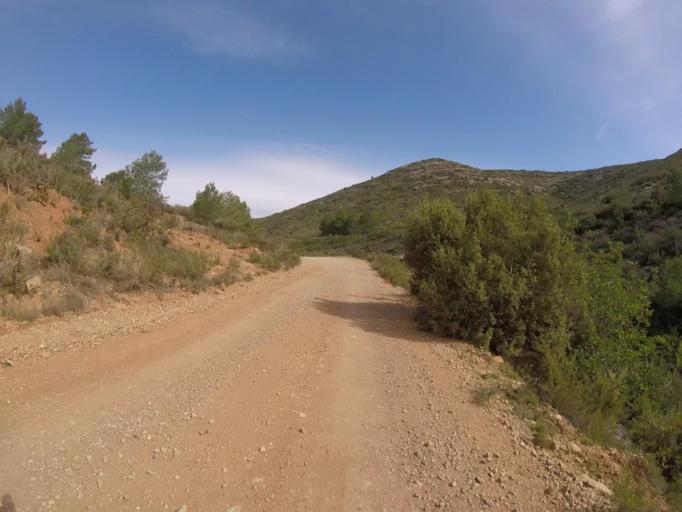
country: ES
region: Valencia
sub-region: Provincia de Castello
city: Torreblanca
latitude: 40.2003
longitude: 0.1538
